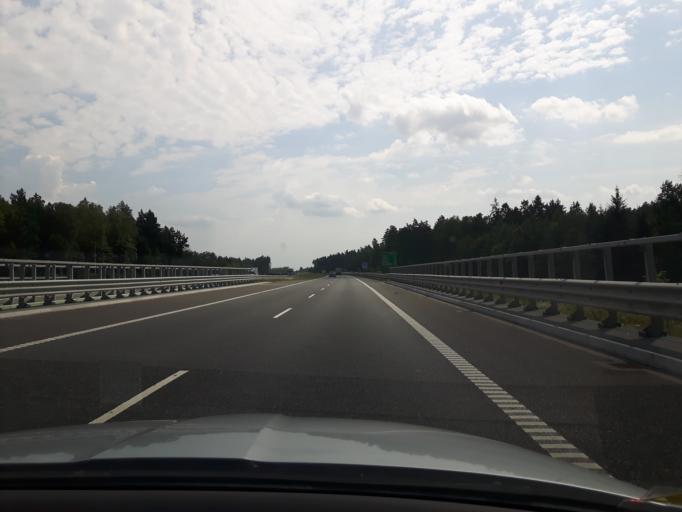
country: PL
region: Warmian-Masurian Voivodeship
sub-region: Powiat olsztynski
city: Olsztynek
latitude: 53.5261
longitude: 20.2812
